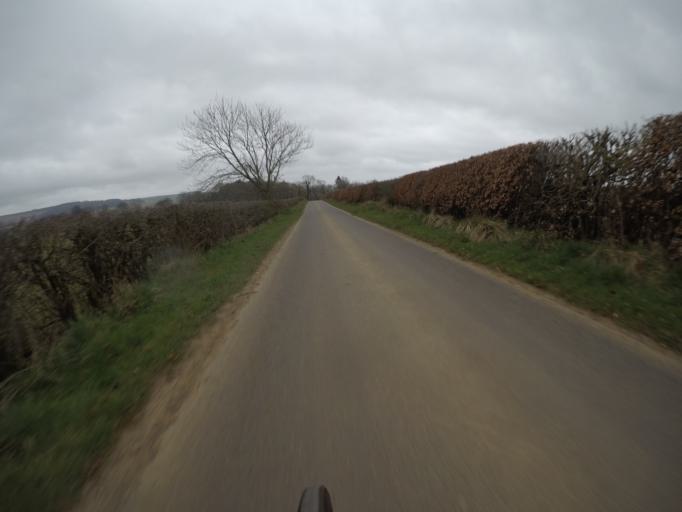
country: GB
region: Scotland
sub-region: East Ayrshire
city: Newmilns
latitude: 55.6175
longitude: -4.3441
